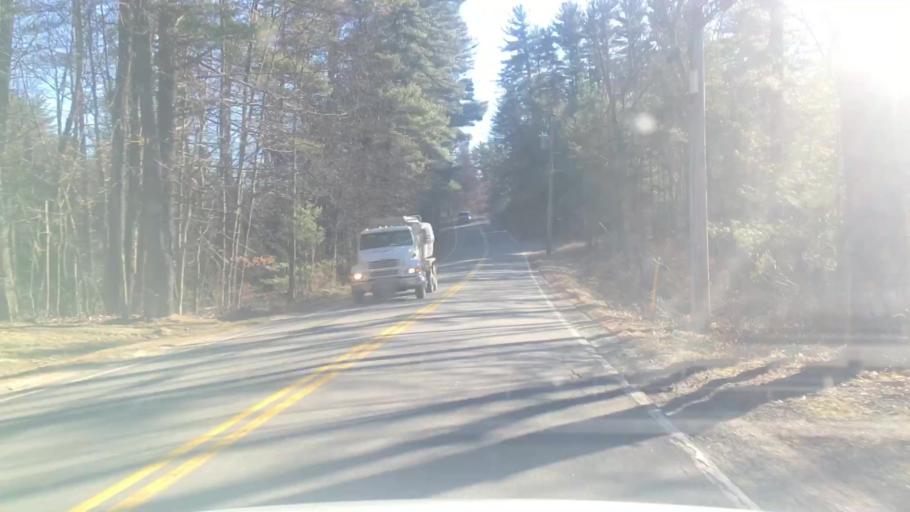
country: US
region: New Hampshire
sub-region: Rockingham County
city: Londonderry
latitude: 42.8906
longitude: -71.4099
